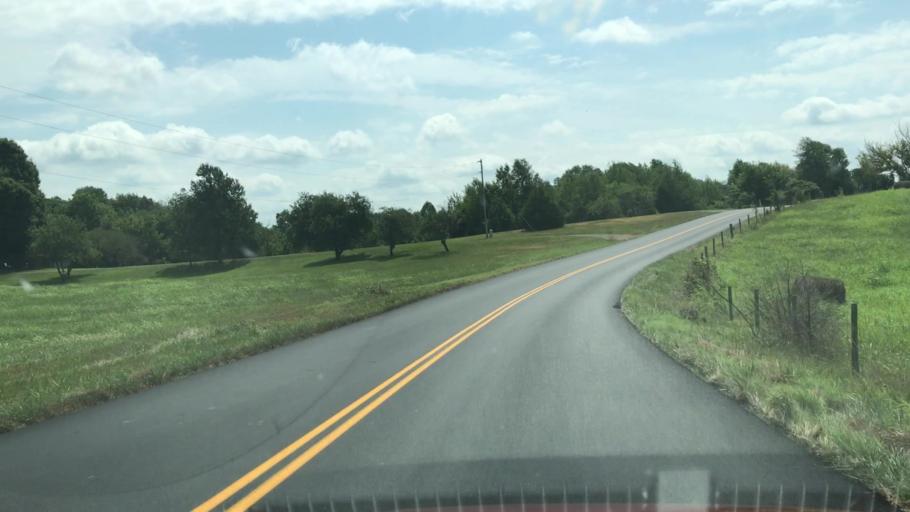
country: US
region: Kentucky
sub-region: Monroe County
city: Tompkinsville
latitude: 36.7502
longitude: -85.7715
